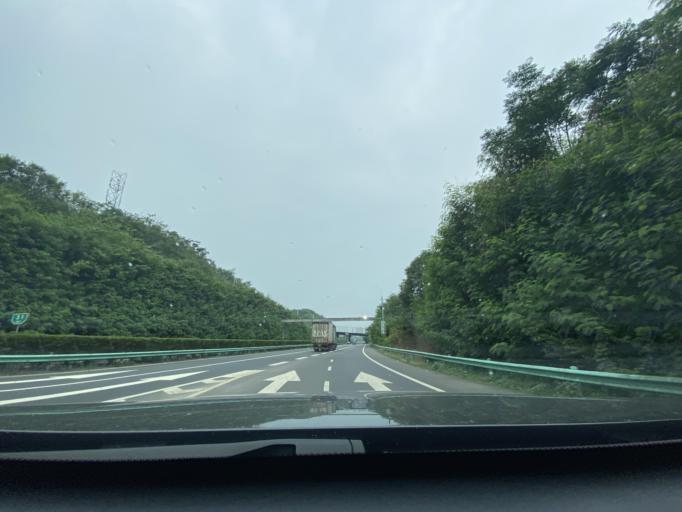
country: CN
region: Sichuan
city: Wenlin
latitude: 30.2980
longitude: 104.1227
